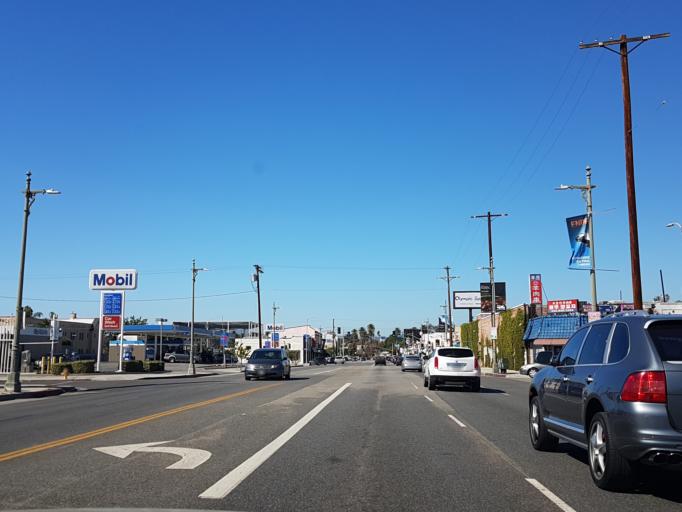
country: US
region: California
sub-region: Los Angeles County
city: Hollywood
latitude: 34.0533
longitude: -118.3191
